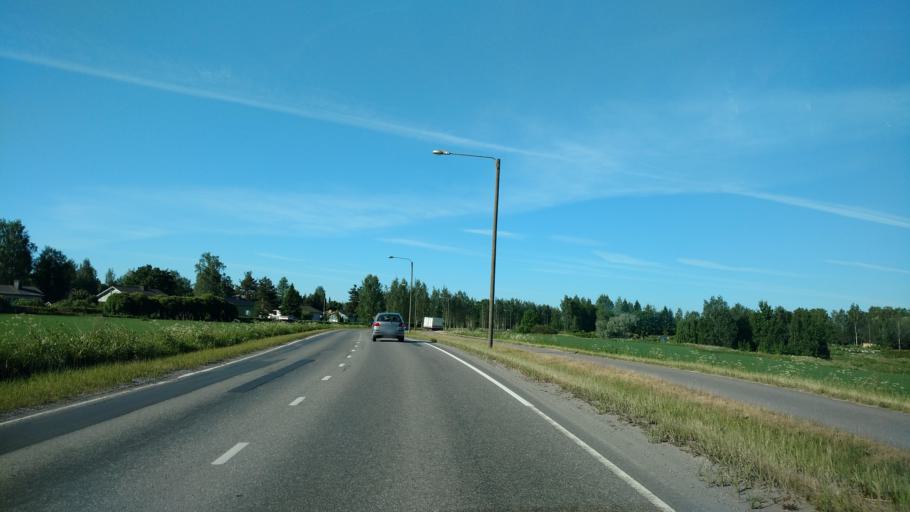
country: FI
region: Varsinais-Suomi
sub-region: Salo
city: Salo
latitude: 60.3981
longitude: 23.1571
